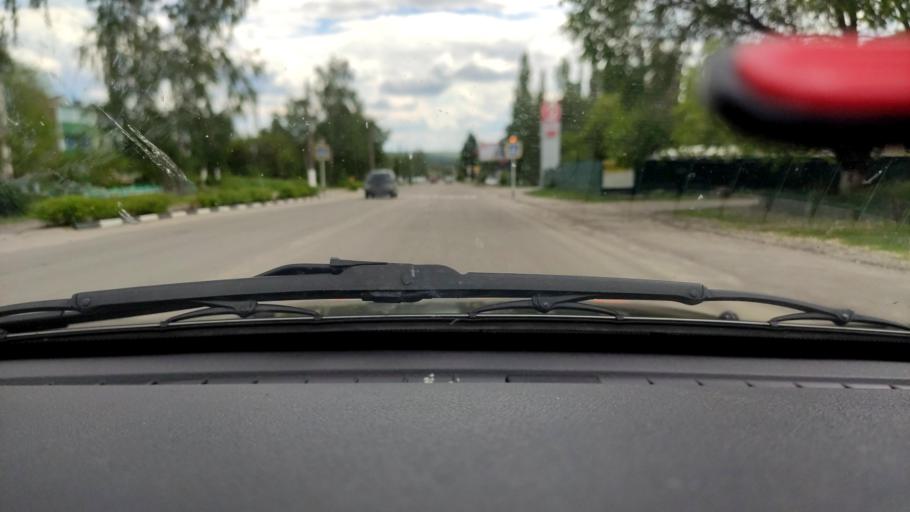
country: RU
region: Voronezj
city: Rossosh'
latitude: 51.0854
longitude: 38.6441
